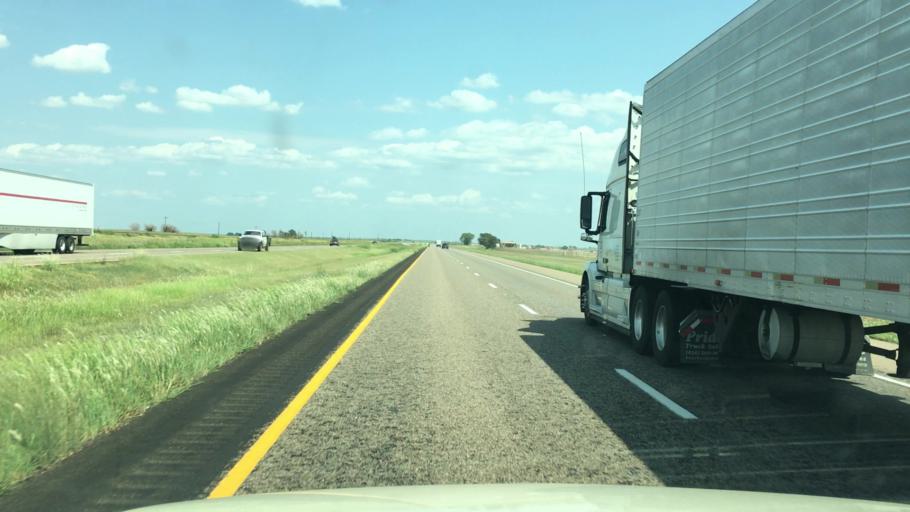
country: US
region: Texas
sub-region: Armstrong County
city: Claude
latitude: 35.0318
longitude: -101.1268
